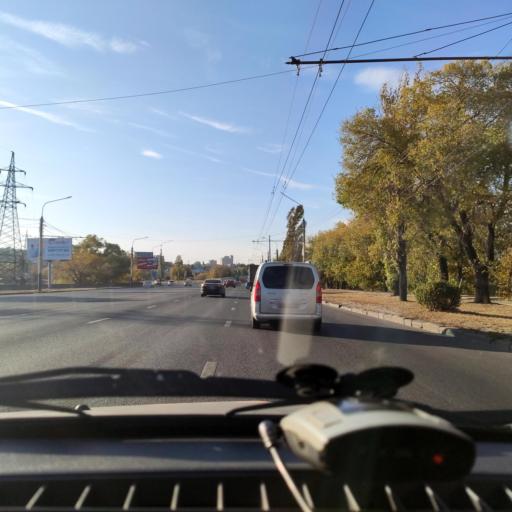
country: RU
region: Voronezj
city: Voronezh
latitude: 51.6358
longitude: 39.2139
